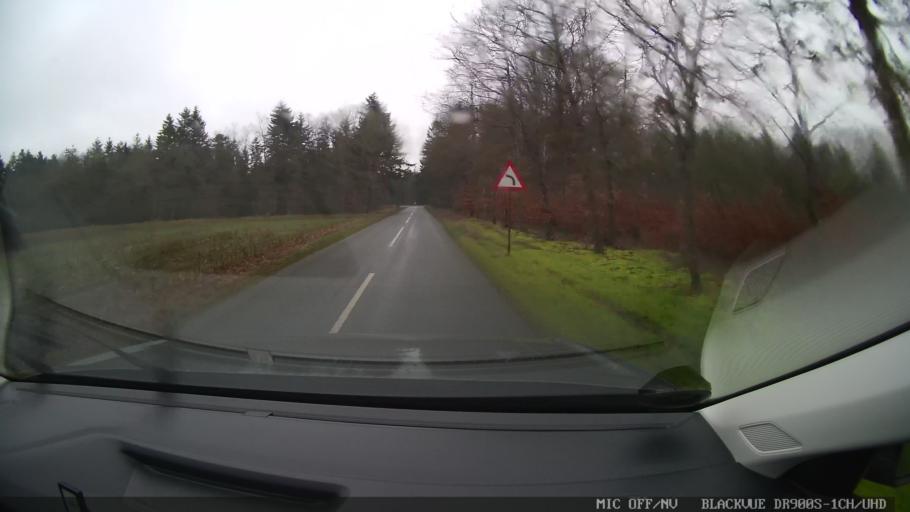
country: DK
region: Central Jutland
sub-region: Viborg Kommune
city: Karup
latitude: 56.2342
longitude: 9.1075
